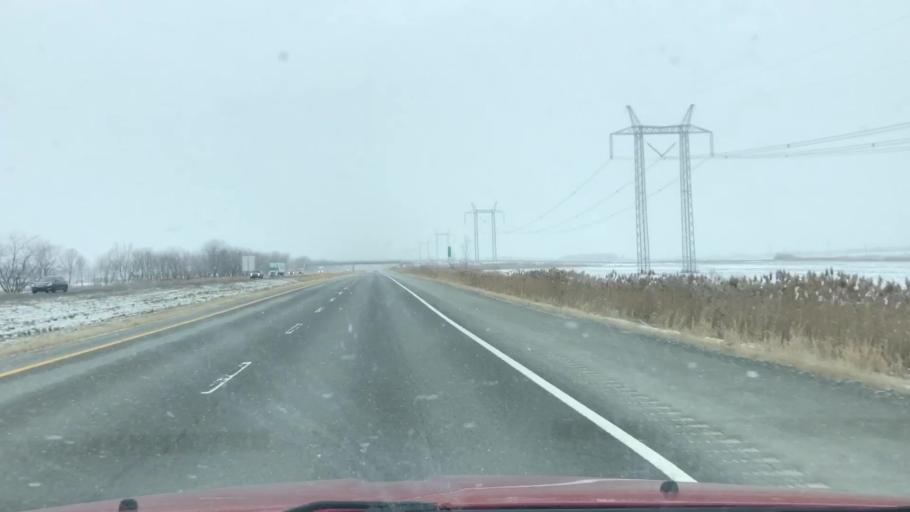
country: CA
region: Quebec
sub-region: Monteregie
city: Rougemont
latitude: 45.3776
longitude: -73.0501
